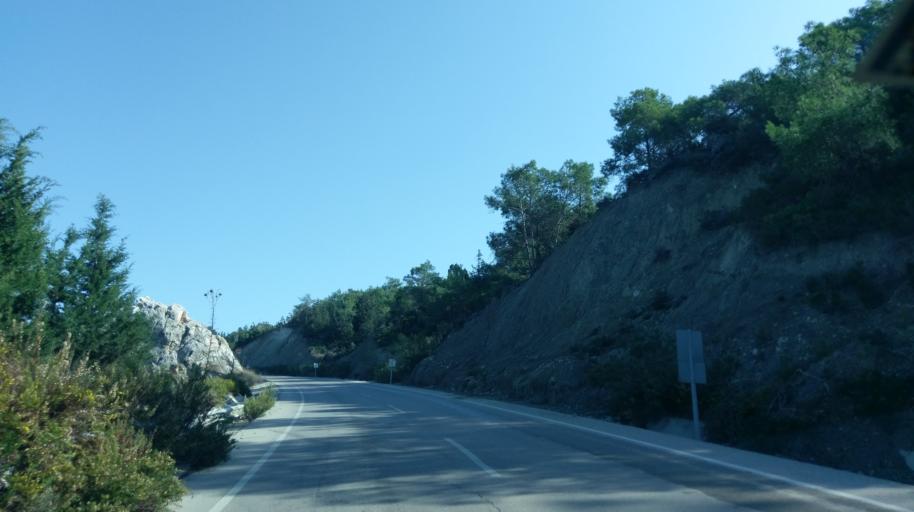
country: CY
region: Ammochostos
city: Trikomo
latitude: 35.4288
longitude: 33.9689
